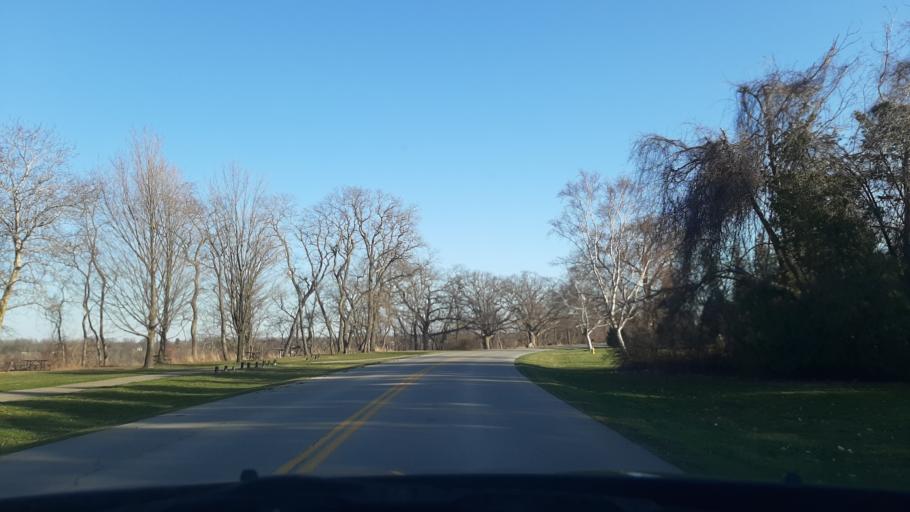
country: US
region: New York
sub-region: Niagara County
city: Youngstown
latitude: 43.2302
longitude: -79.0600
